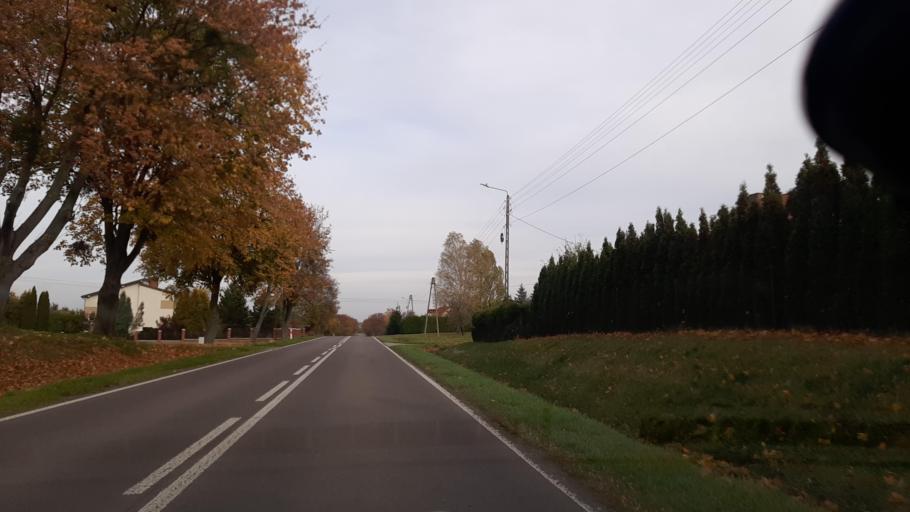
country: PL
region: Lublin Voivodeship
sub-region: Powiat pulawski
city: Markuszow
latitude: 51.3477
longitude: 22.2670
